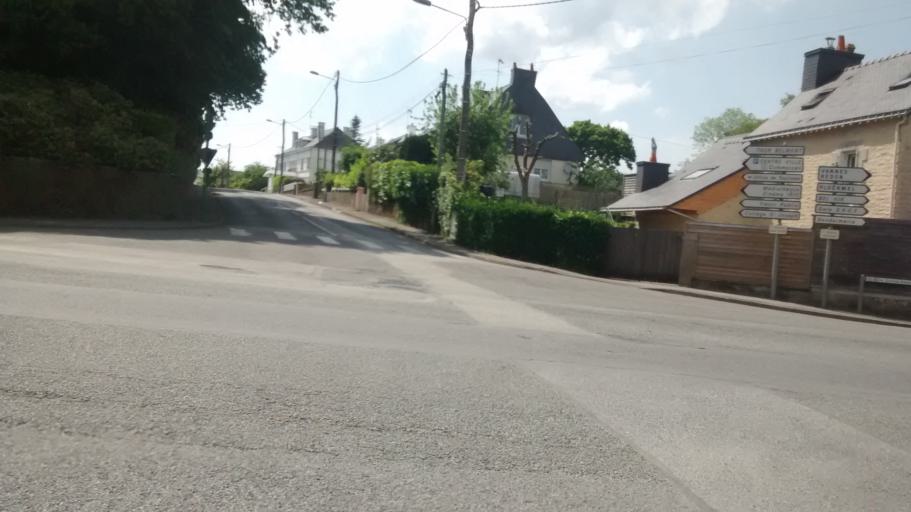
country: FR
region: Brittany
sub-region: Departement du Morbihan
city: Questembert
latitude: 47.6640
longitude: -2.4499
